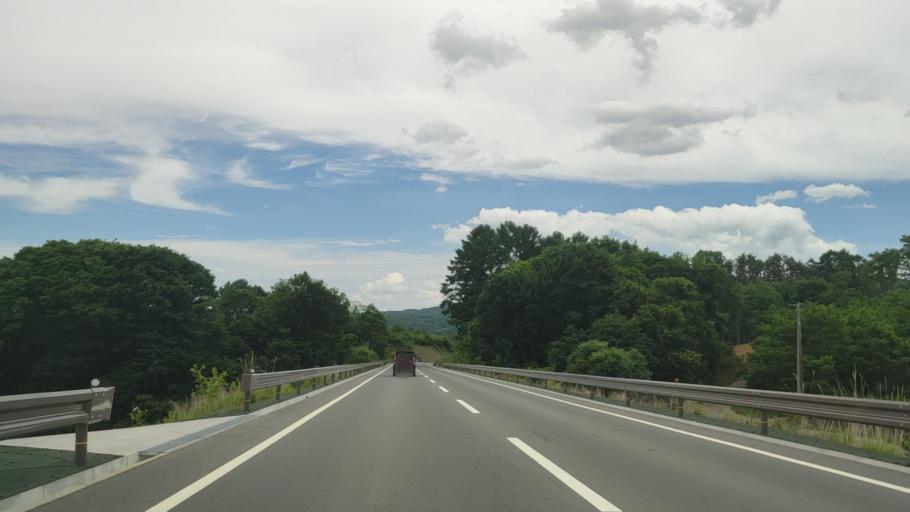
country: JP
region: Nagano
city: Kamimaruko
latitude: 36.2753
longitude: 138.3006
